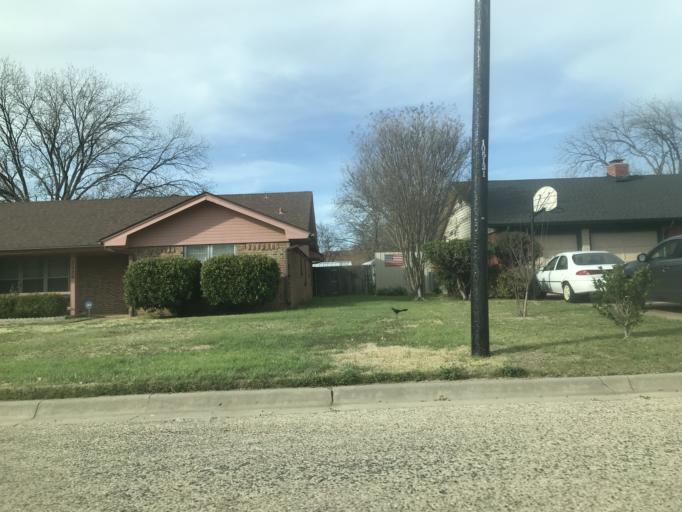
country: US
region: Texas
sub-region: Taylor County
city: Abilene
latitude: 32.4143
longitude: -99.7661
